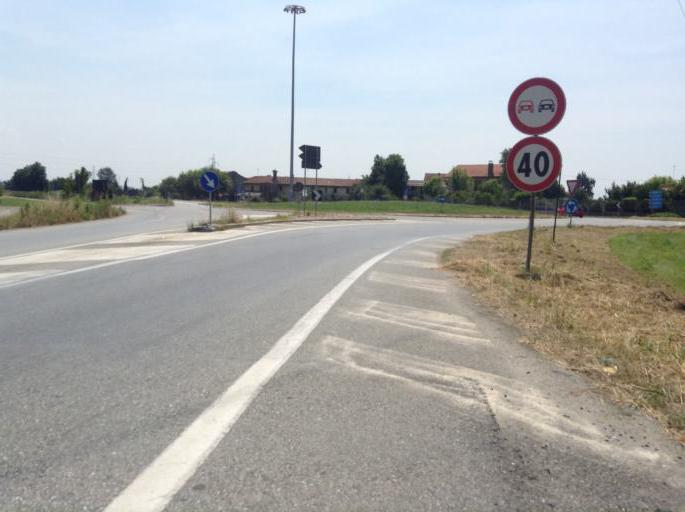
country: IT
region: Piedmont
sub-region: Provincia di Torino
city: Carignano
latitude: 44.8950
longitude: 7.6725
